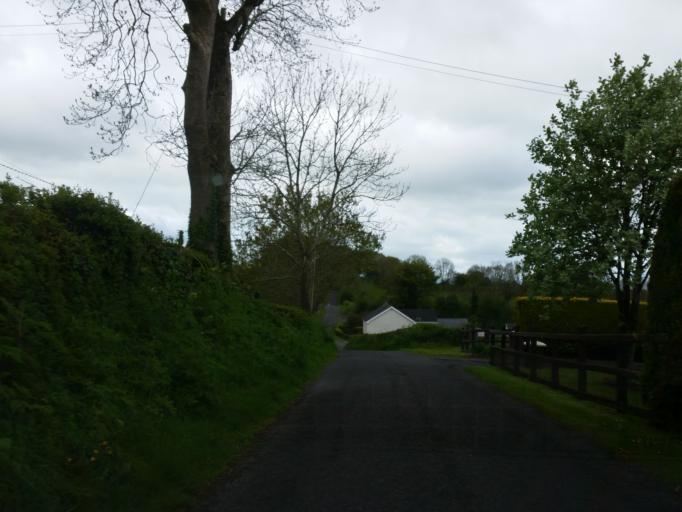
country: GB
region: Northern Ireland
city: Fivemiletown
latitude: 54.3297
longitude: -7.3856
